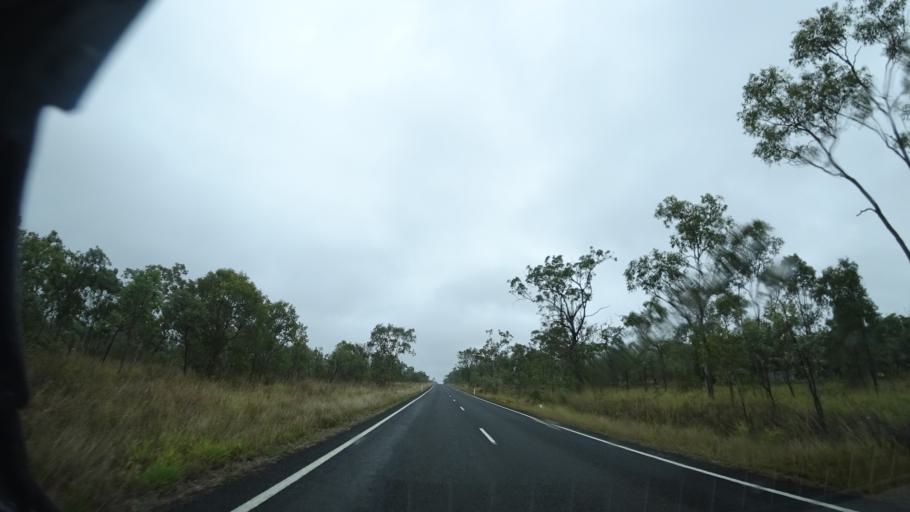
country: AU
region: Queensland
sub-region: Tablelands
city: Ravenshoe
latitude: -17.6980
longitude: 145.1904
